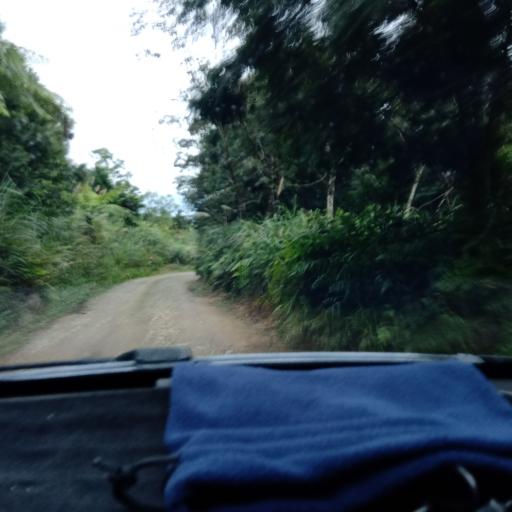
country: TW
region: Taiwan
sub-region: Yilan
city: Yilan
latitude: 24.8101
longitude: 121.6917
